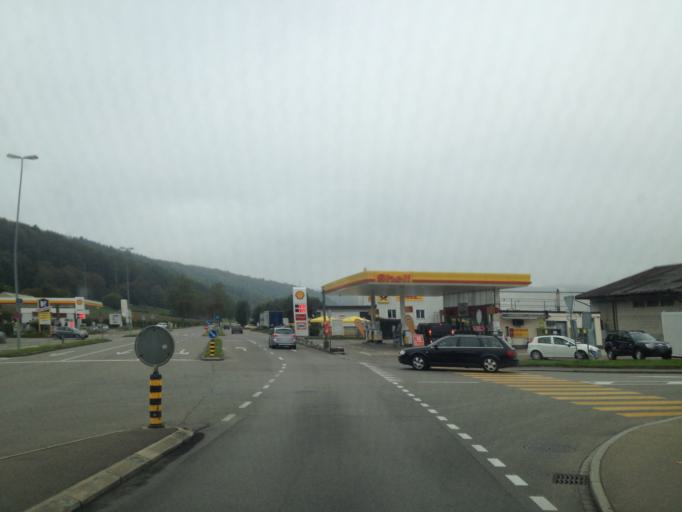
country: CH
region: Schaffhausen
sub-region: Bezirk Reiat
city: Thayngen
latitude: 47.7407
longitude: 8.7167
